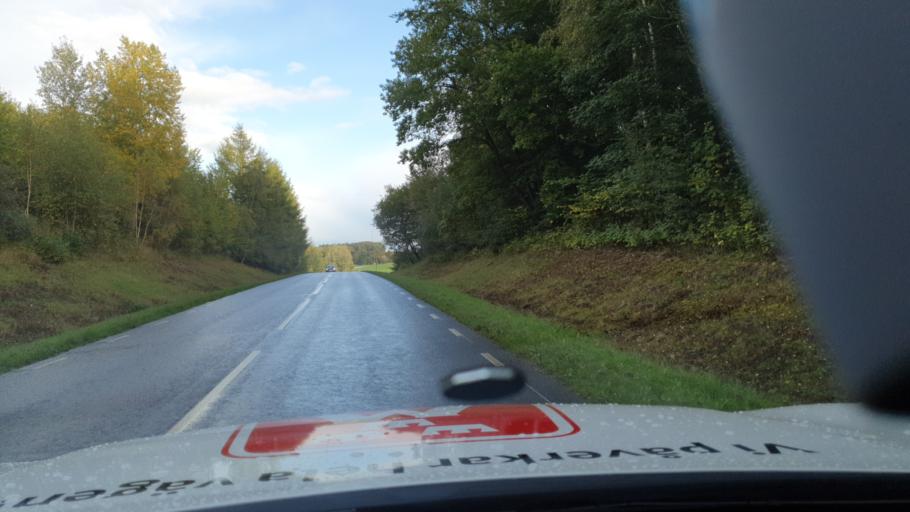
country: SE
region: Skane
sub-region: Malmo
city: Oxie
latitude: 55.5481
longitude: 13.1449
